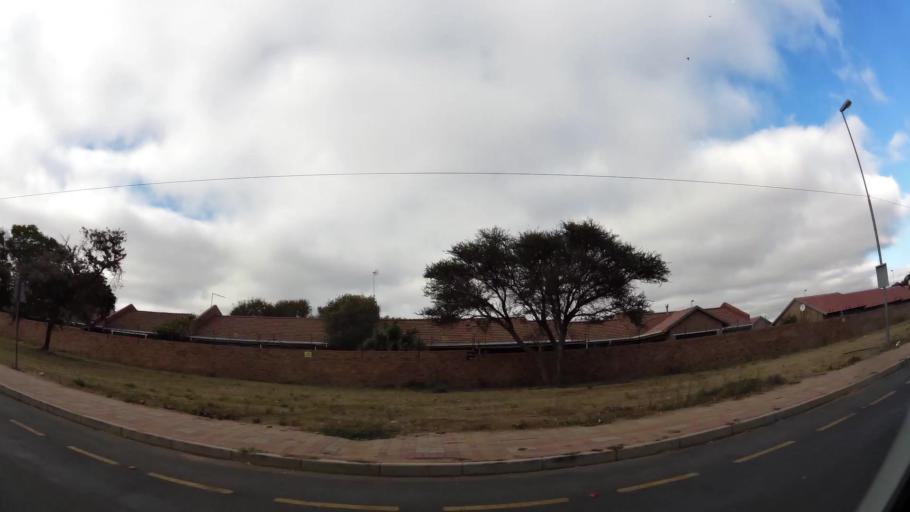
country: ZA
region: Limpopo
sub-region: Capricorn District Municipality
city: Polokwane
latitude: -23.9170
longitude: 29.4714
